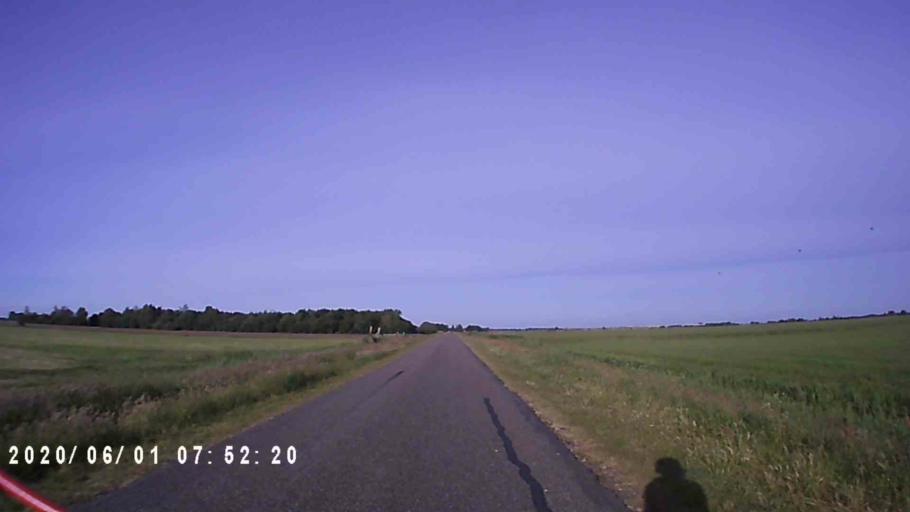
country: NL
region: Friesland
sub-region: Gemeente Dantumadiel
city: Rinsumageast
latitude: 53.2842
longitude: 5.9409
